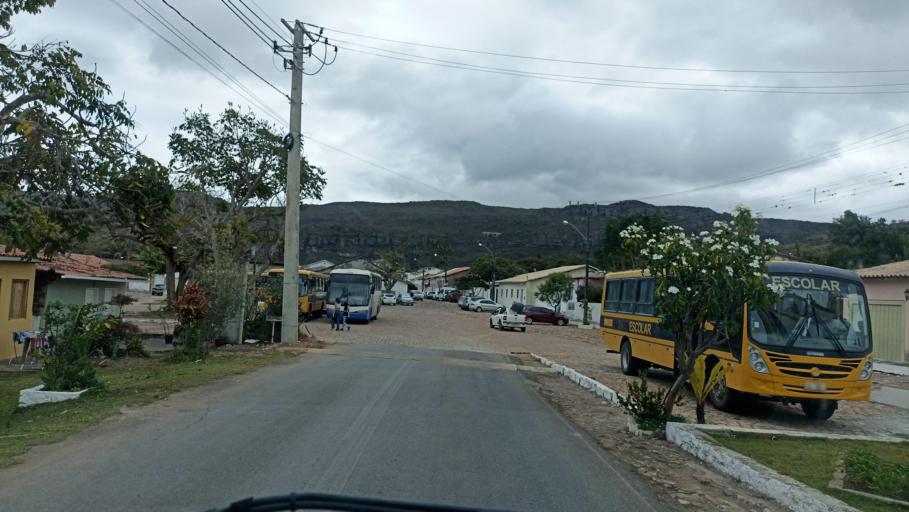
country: BR
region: Bahia
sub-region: Andarai
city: Vera Cruz
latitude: -13.0037
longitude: -41.3674
